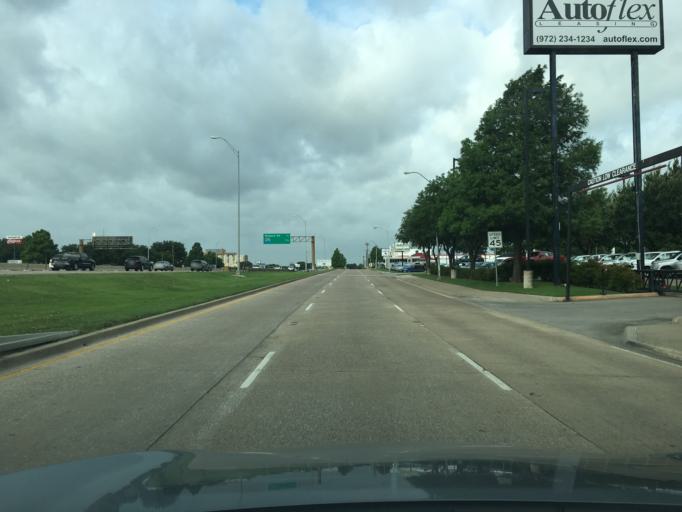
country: US
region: Texas
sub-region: Dallas County
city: Richardson
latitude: 32.9457
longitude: -96.7391
